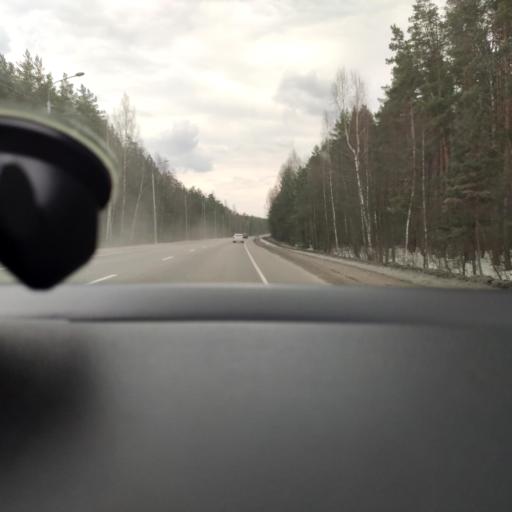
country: RU
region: Moskovskaya
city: Il'inskiy Pogost
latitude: 55.4752
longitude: 38.9513
